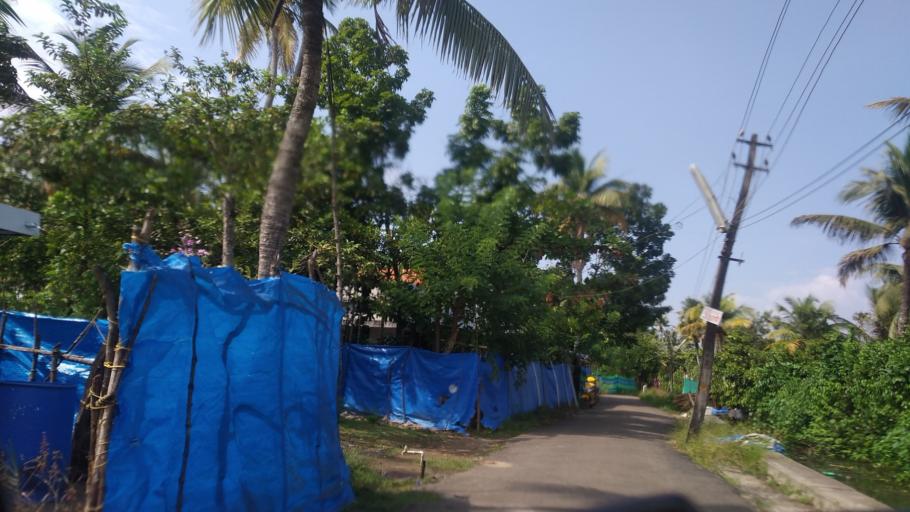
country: IN
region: Kerala
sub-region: Ernakulam
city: Elur
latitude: 10.0821
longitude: 76.2019
